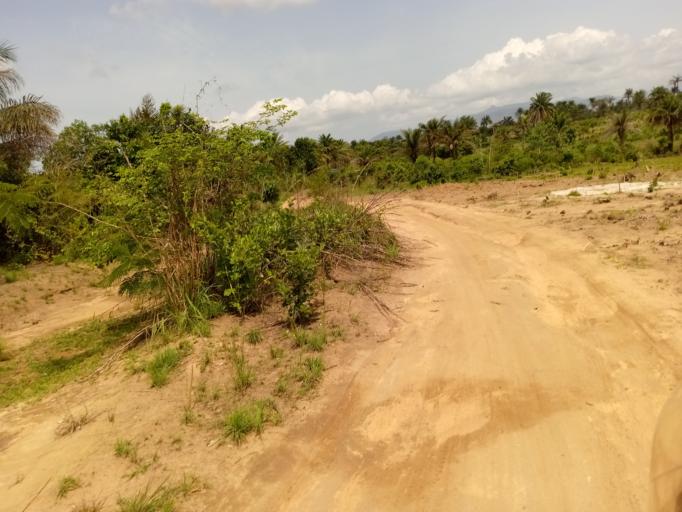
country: SL
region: Western Area
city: Waterloo
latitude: 8.3586
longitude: -13.0041
